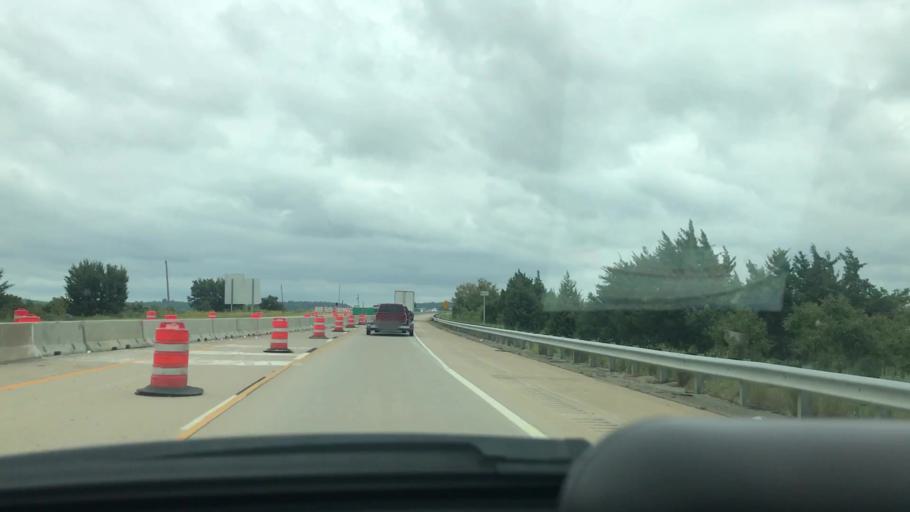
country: US
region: Oklahoma
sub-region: McIntosh County
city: Eufaula
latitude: 35.2201
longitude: -95.6083
